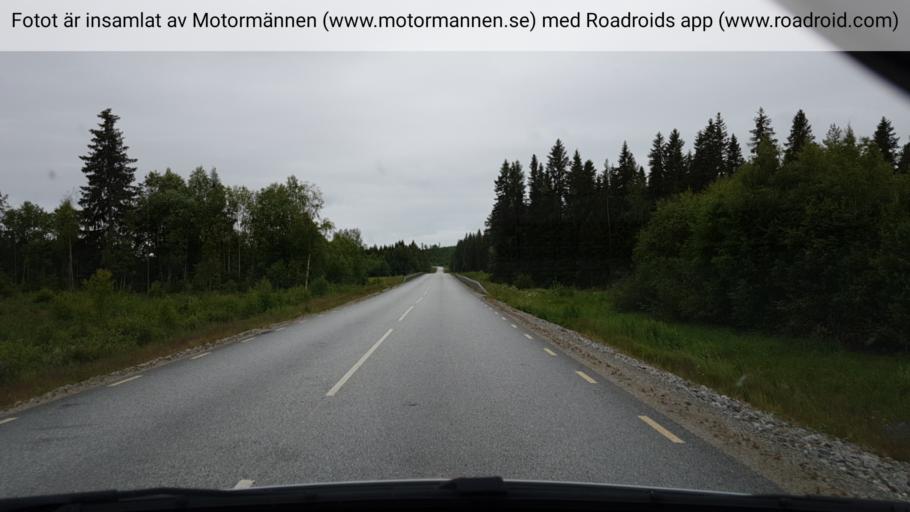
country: SE
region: Vaesterbotten
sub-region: Vindelns Kommun
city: Vindeln
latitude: 64.1919
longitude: 19.4088
